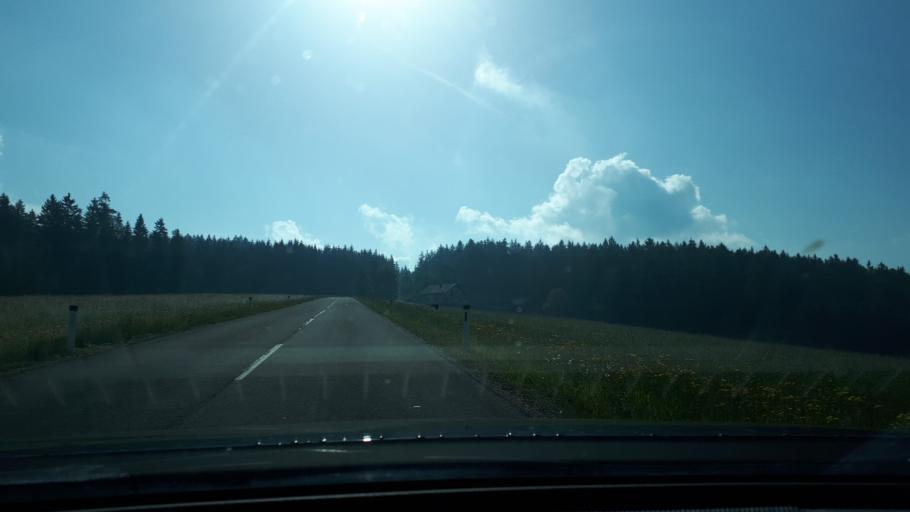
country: AT
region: Carinthia
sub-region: Politischer Bezirk Wolfsberg
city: Preitenegg
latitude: 46.9324
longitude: 14.9728
